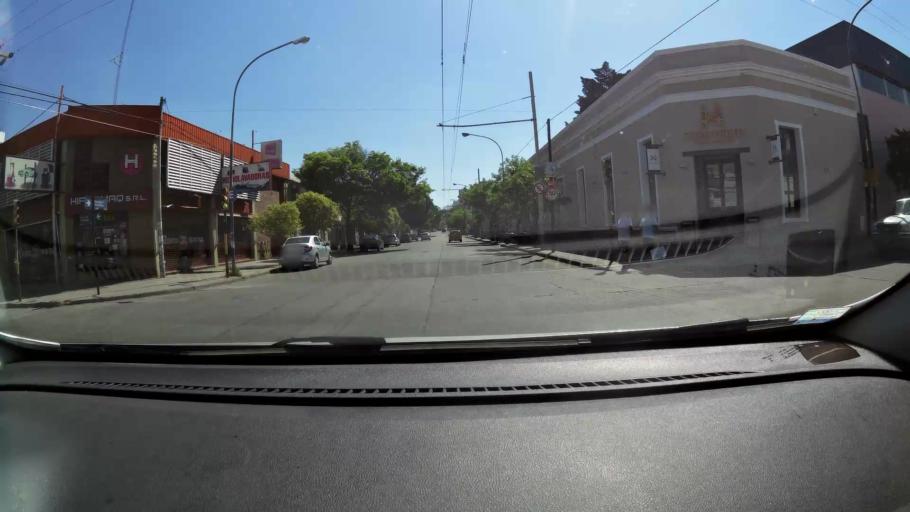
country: AR
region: Cordoba
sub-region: Departamento de Capital
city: Cordoba
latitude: -31.4109
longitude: -64.1683
